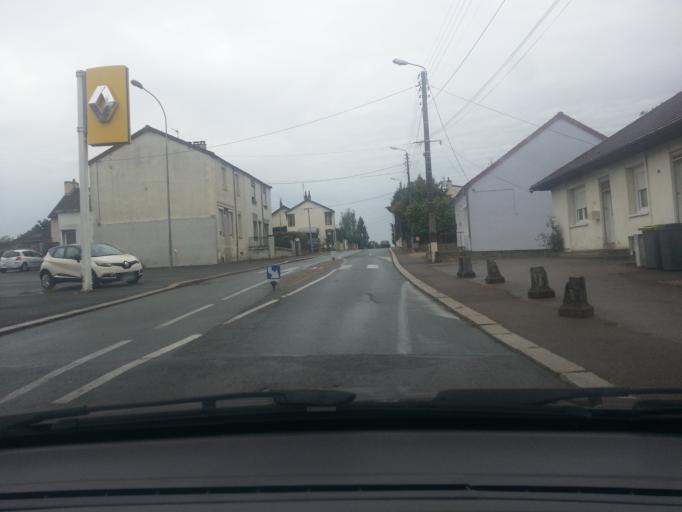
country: FR
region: Bourgogne
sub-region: Departement de Saone-et-Loire
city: Montchanin
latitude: 46.7424
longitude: 4.4727
